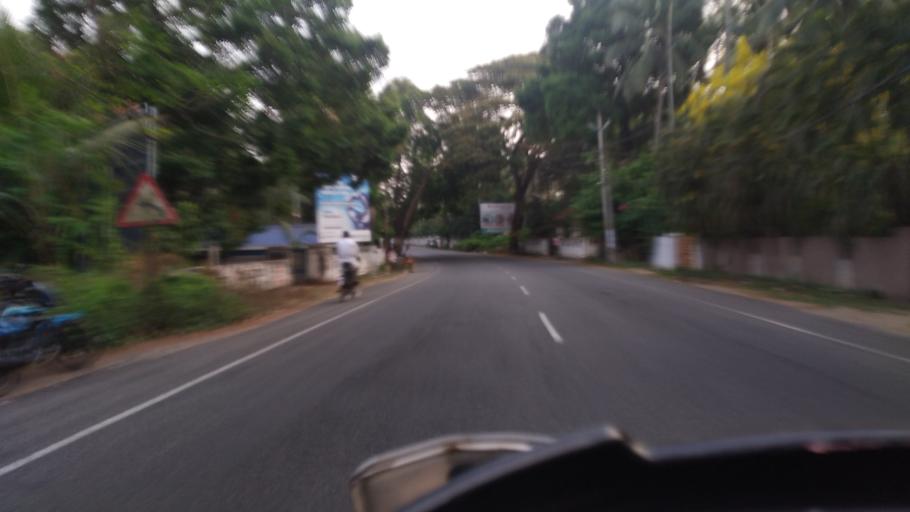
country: IN
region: Kerala
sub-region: Thrissur District
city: Kodungallur
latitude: 10.2505
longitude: 76.1864
